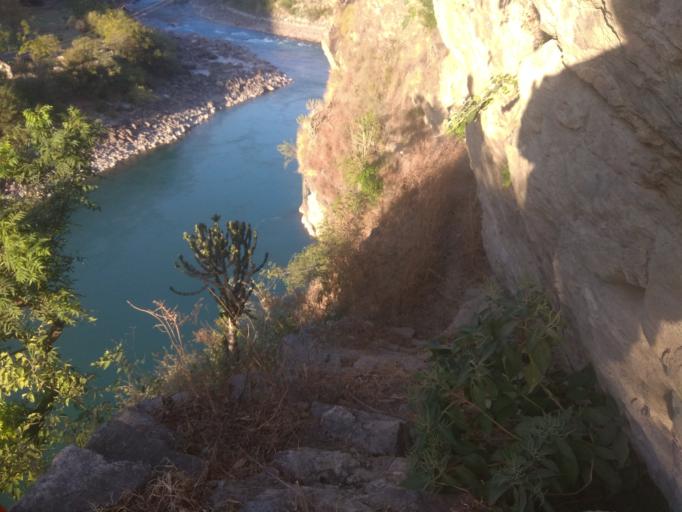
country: NP
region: Mid Western
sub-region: Bheri Zone
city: Dailekh
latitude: 29.2784
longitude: 81.7319
